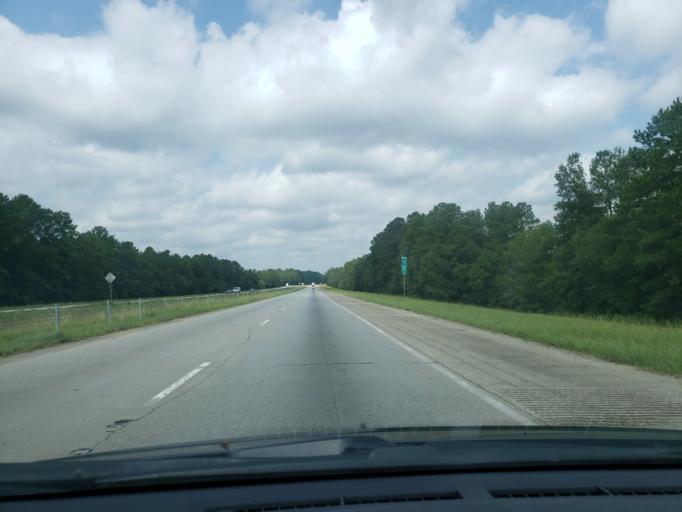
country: US
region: Georgia
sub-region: Emanuel County
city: Swainsboro
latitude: 32.4082
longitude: -82.3378
